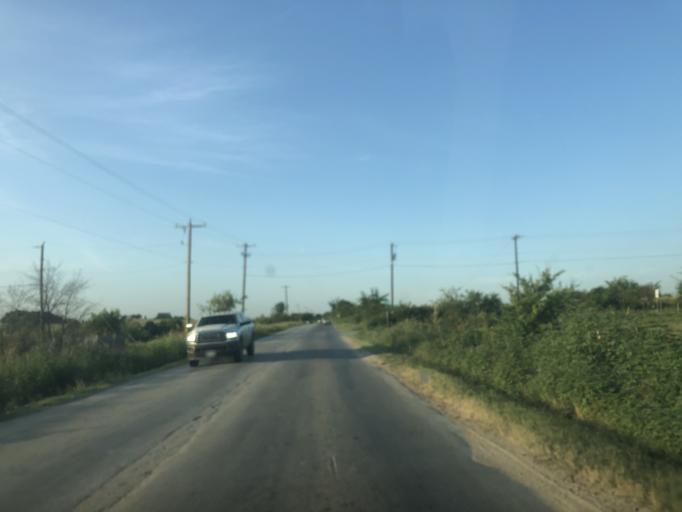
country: US
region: Texas
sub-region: Tarrant County
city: White Settlement
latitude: 32.7794
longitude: -97.4869
